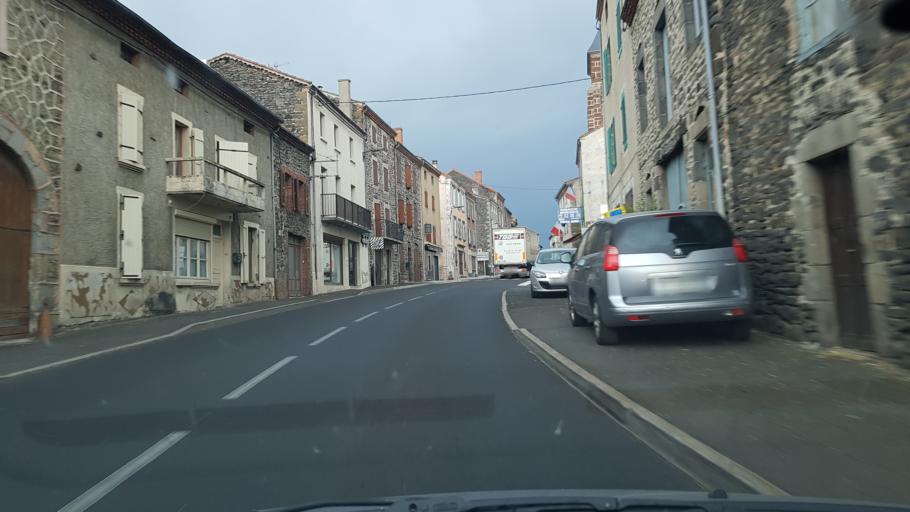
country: FR
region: Auvergne
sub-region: Departement de la Haute-Loire
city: Paulhaguet
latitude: 45.1571
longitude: 3.5400
